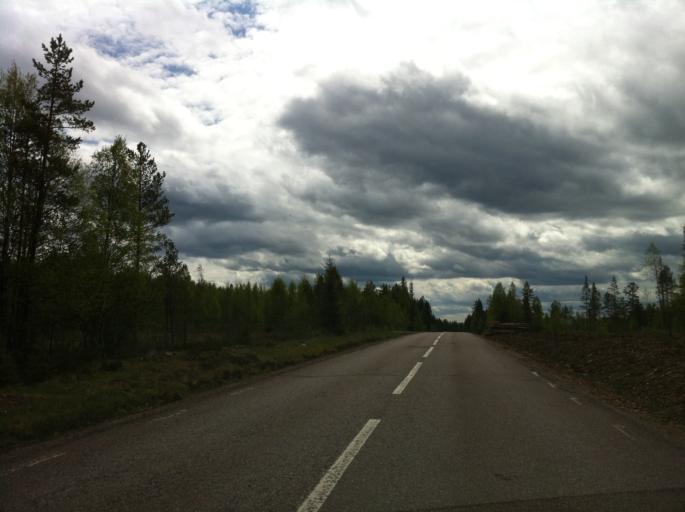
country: NO
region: Hedmark
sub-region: Trysil
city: Innbygda
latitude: 61.5369
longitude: 13.0822
